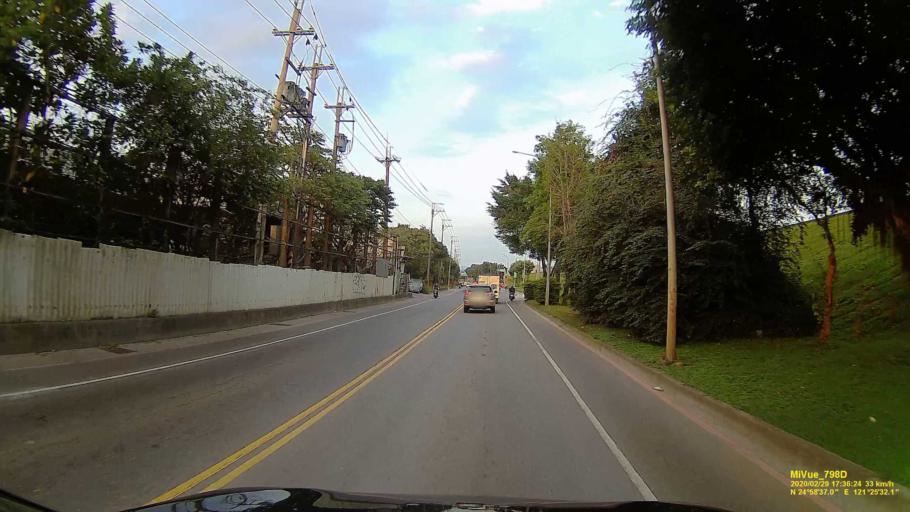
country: TW
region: Taipei
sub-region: Taipei
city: Banqiao
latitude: 24.9772
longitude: 121.4259
